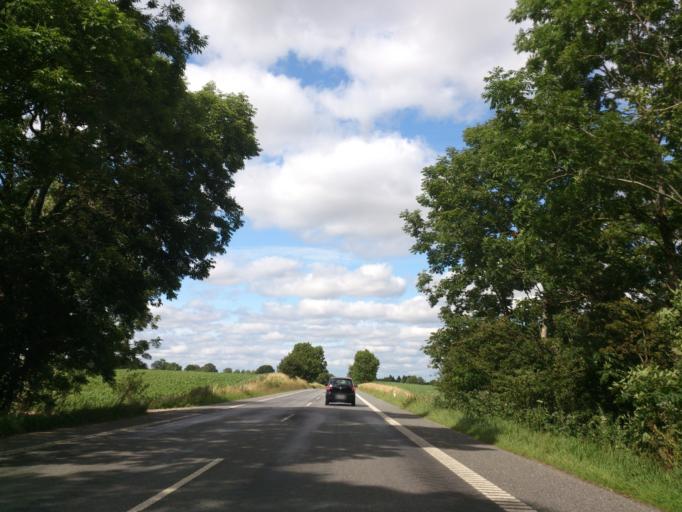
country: DK
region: South Denmark
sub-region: Aabenraa Kommune
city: Krusa
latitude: 54.9152
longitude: 9.4434
